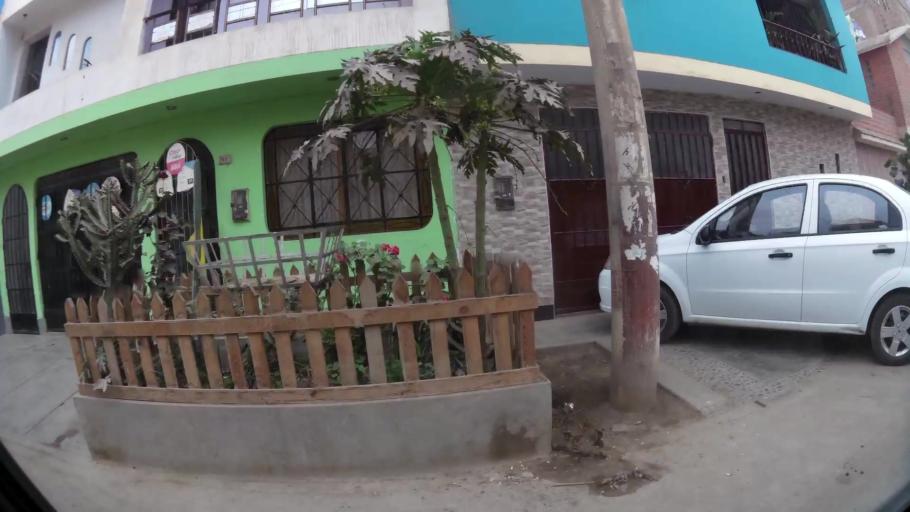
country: PE
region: Lima
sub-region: Lima
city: Independencia
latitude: -11.9685
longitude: -77.0919
